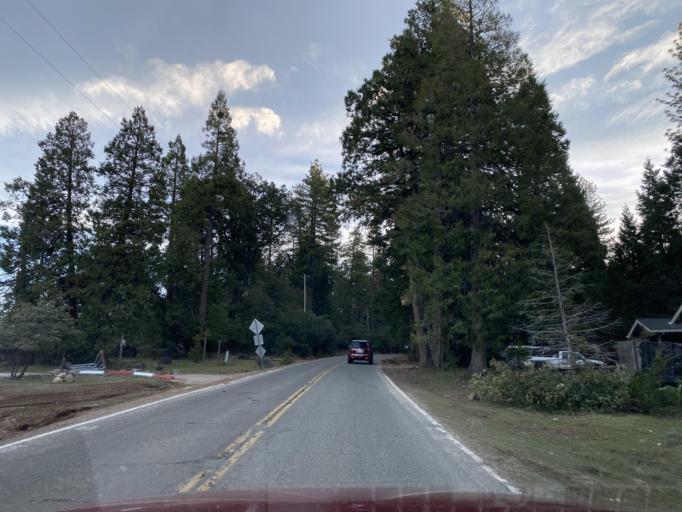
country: US
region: California
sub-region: Amador County
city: Pioneer
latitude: 38.4940
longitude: -120.5868
